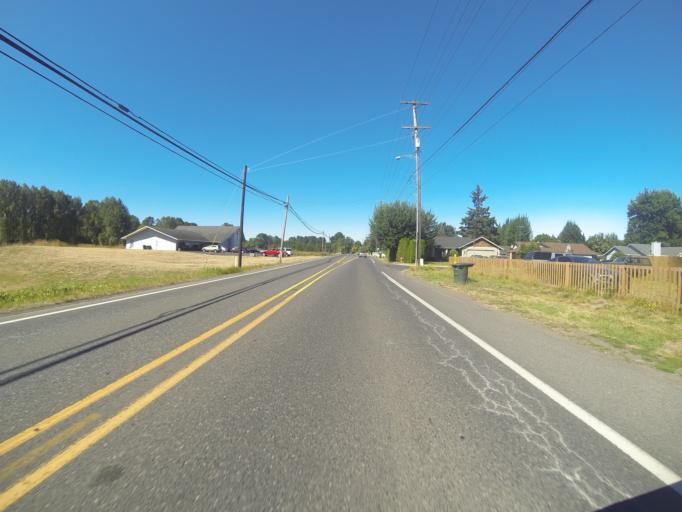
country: US
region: Washington
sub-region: Cowlitz County
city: Woodland
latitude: 45.9197
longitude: -122.7288
